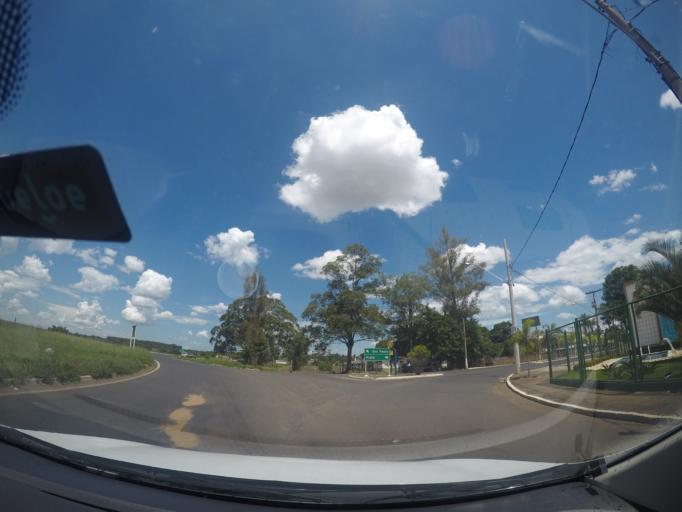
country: BR
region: Minas Gerais
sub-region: Prata
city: Prata
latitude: -19.2976
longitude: -48.9084
